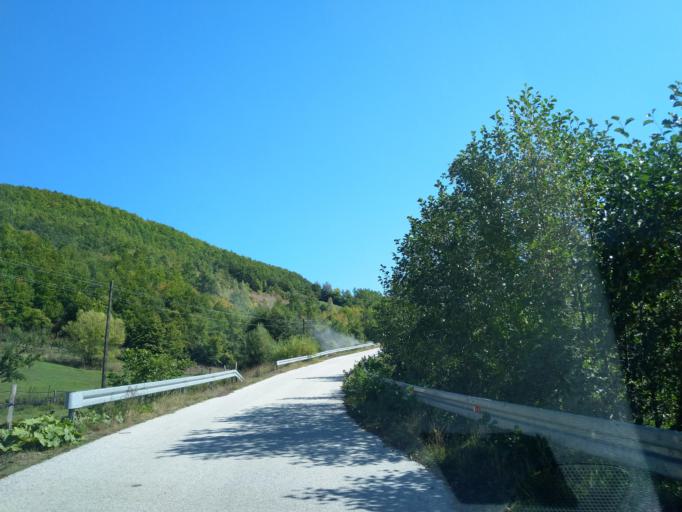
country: RS
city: Sokolovica
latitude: 43.2604
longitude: 20.2987
